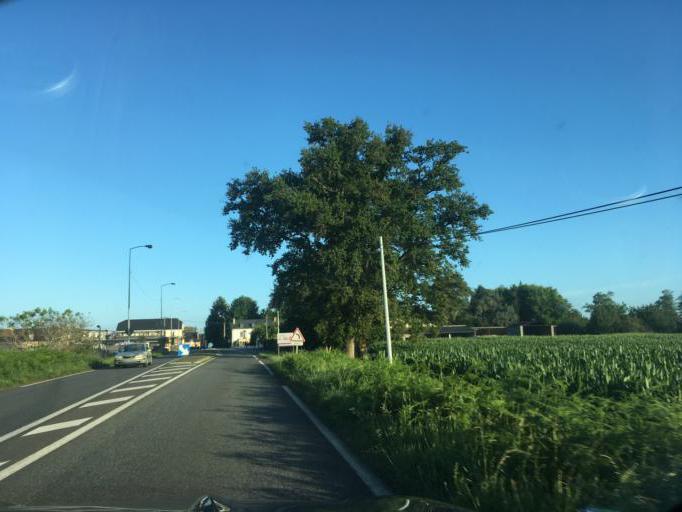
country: FR
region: Aquitaine
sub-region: Departement des Pyrenees-Atlantiques
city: Soumoulou
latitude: 43.2594
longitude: -0.1569
